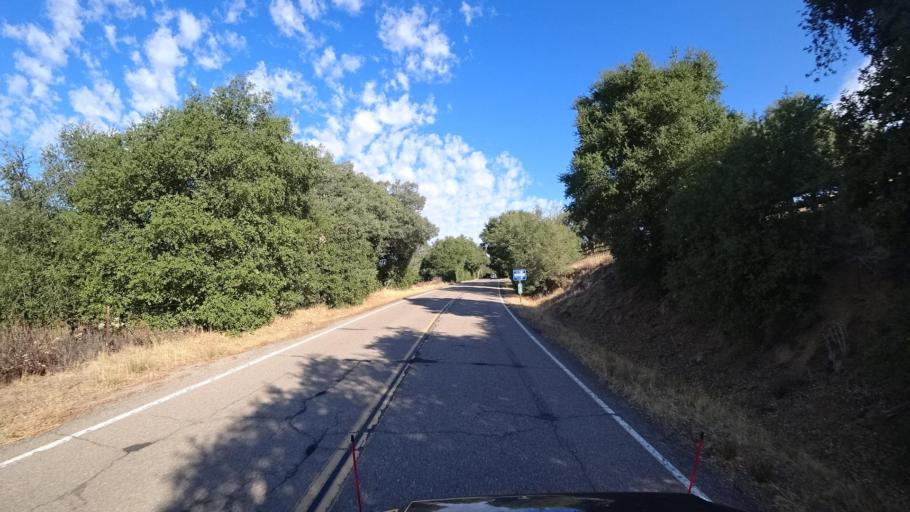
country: US
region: California
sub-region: San Diego County
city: Julian
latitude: 33.1505
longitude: -116.7097
